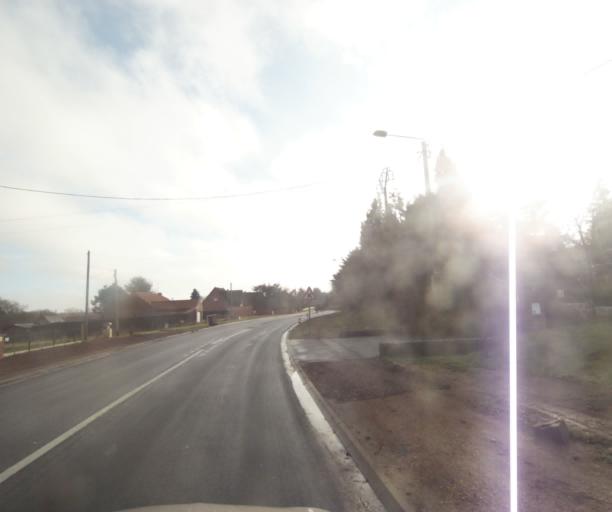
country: FR
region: Nord-Pas-de-Calais
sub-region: Departement du Nord
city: Saulzoir
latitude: 50.2703
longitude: 3.4622
